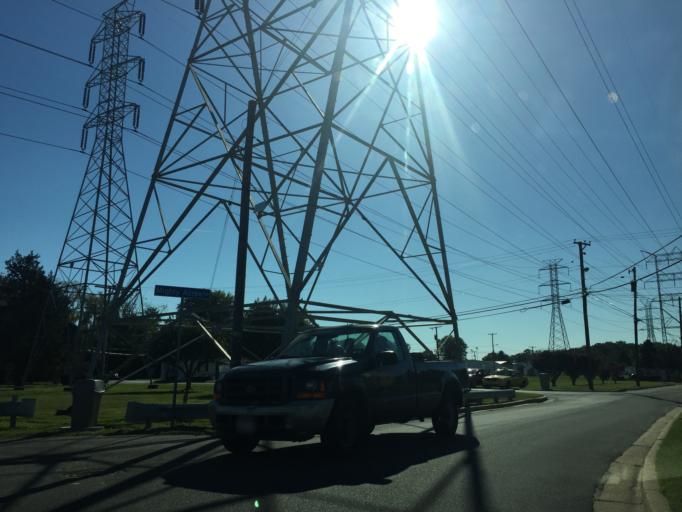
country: US
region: Maryland
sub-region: Baltimore County
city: Dundalk
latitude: 39.2561
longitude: -76.5028
